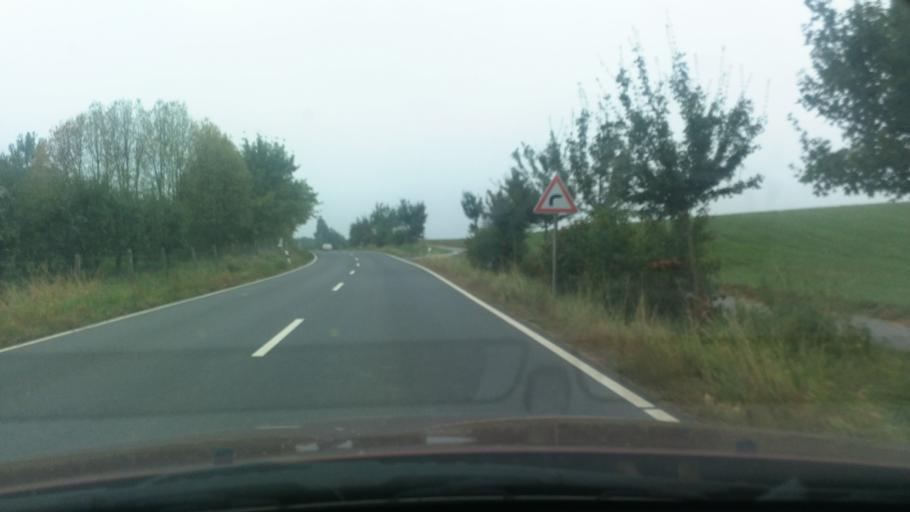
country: DE
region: Saxony
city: Goerlitz
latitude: 51.1255
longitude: 14.9413
